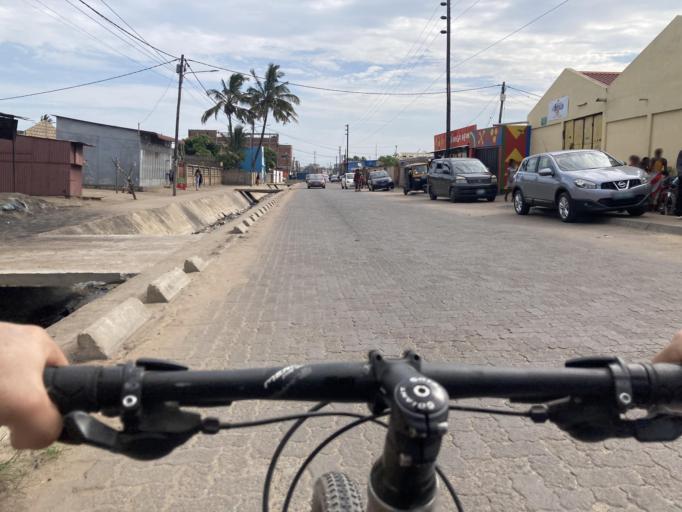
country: MZ
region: Maputo City
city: Maputo
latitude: -25.9436
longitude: 32.5833
